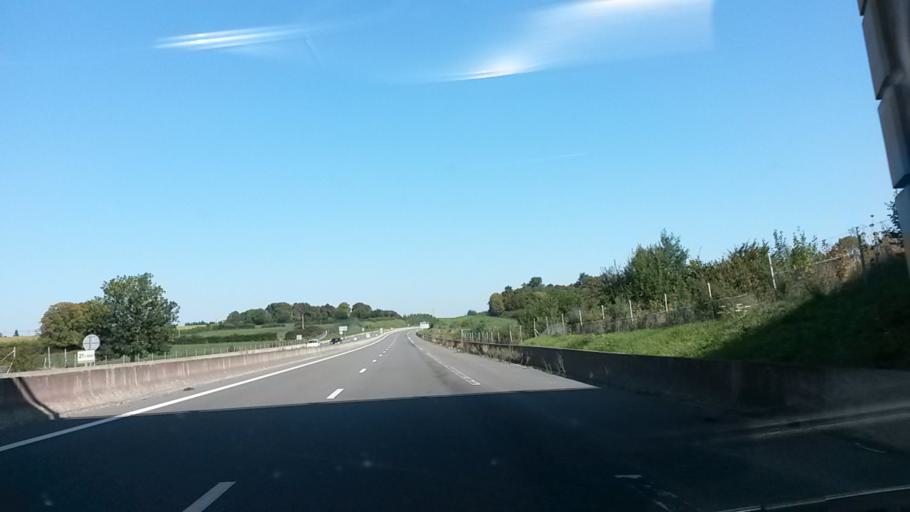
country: FR
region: Nord-Pas-de-Calais
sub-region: Departement du Nord
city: Hautmont
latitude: 50.2113
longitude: 3.9539
